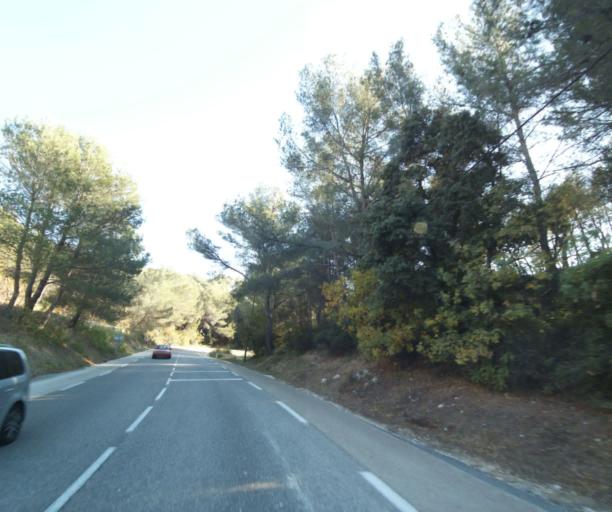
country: FR
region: Provence-Alpes-Cote d'Azur
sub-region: Departement des Bouches-du-Rhone
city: La Ciotat
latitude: 43.2036
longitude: 5.5885
